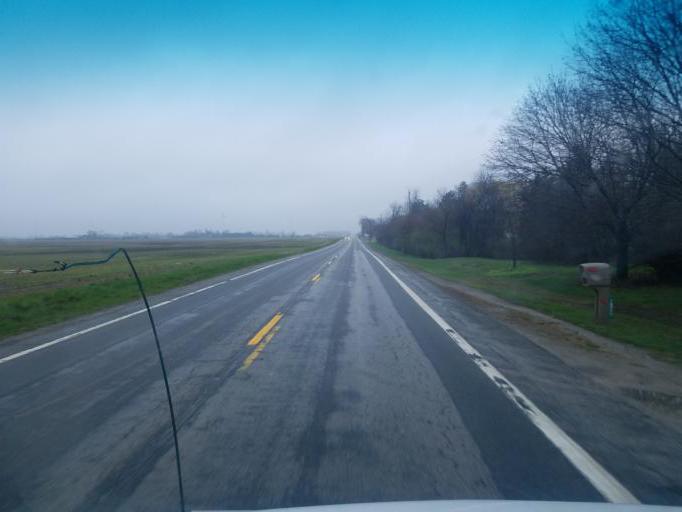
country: US
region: Ohio
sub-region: Wood County
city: Weston
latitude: 41.3724
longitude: -83.7641
